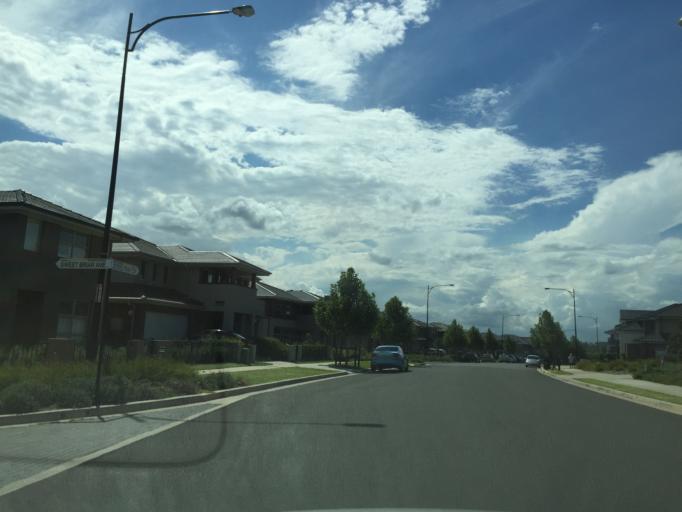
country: AU
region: New South Wales
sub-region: Blacktown
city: Doonside
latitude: -33.7787
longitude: 150.8699
